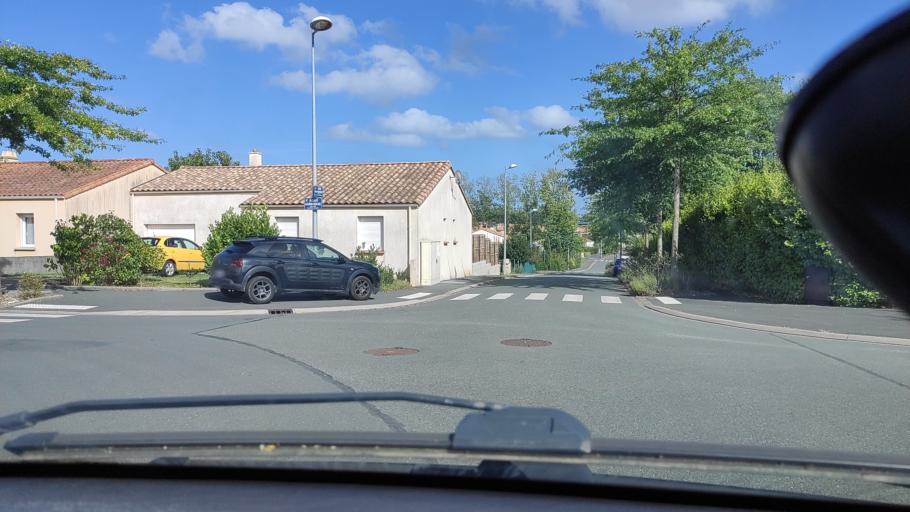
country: FR
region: Pays de la Loire
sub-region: Departement de la Vendee
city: La Roche-sur-Yon
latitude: 46.6890
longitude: -1.4528
